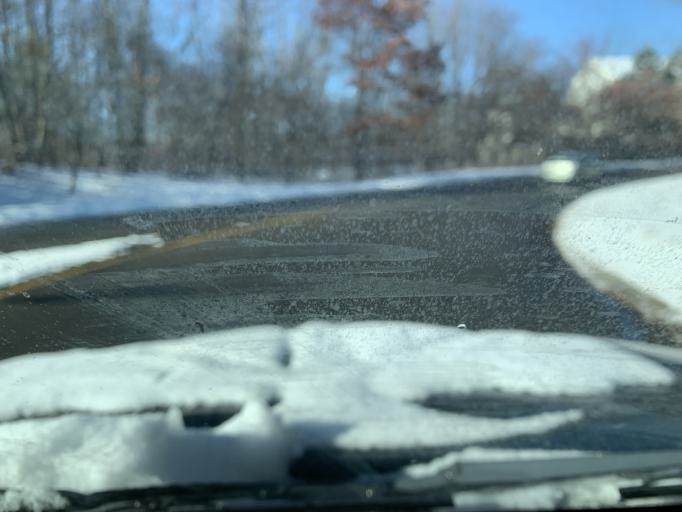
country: US
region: Massachusetts
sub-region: Essex County
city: Danvers
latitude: 42.5609
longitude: -70.9779
